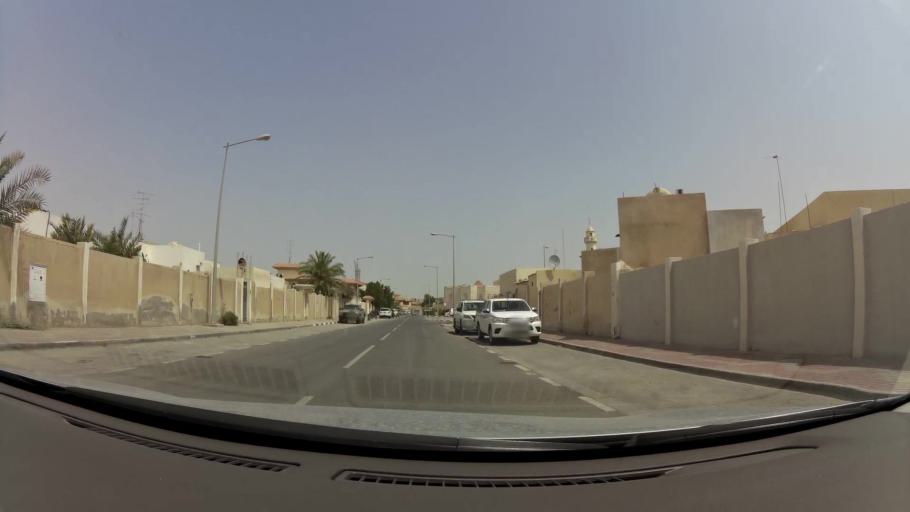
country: QA
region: Baladiyat ar Rayyan
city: Ar Rayyan
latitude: 25.2478
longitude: 51.4251
